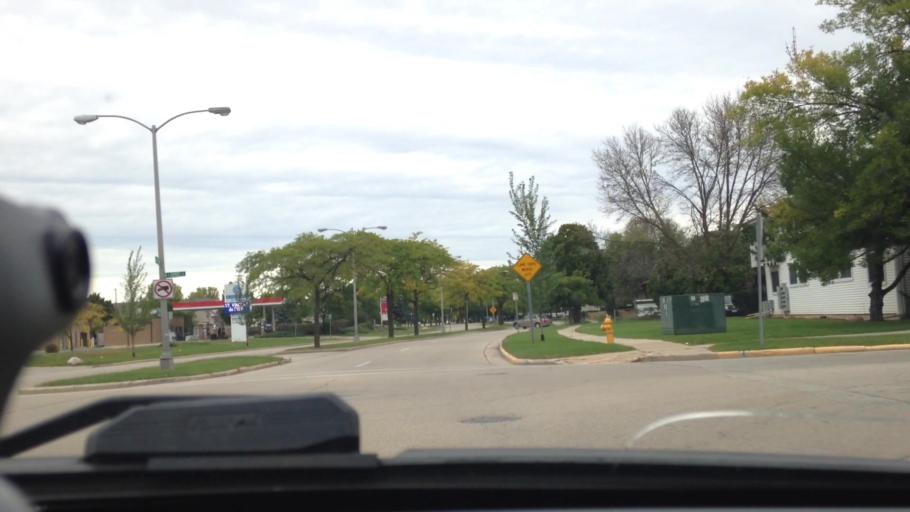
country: US
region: Wisconsin
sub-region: Fond du Lac County
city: North Fond du Lac
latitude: 43.7876
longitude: -88.4730
